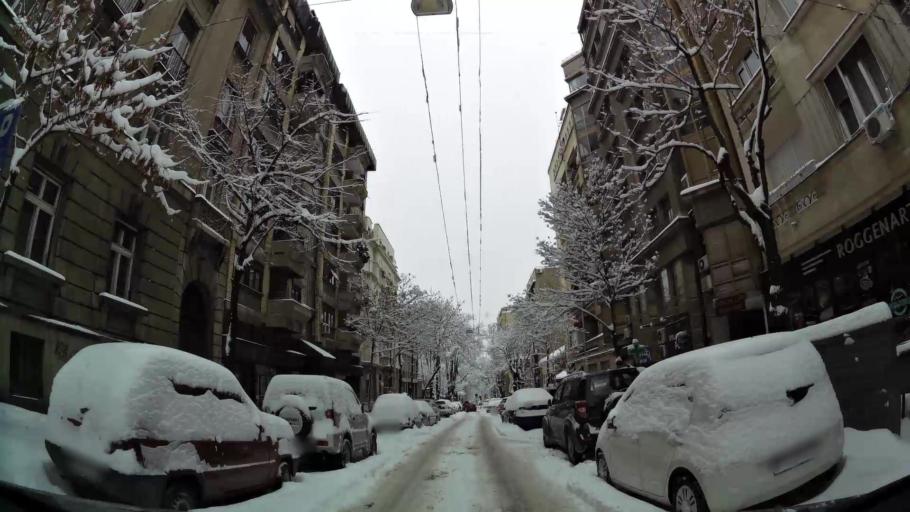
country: RS
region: Central Serbia
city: Belgrade
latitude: 44.8068
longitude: 20.4677
